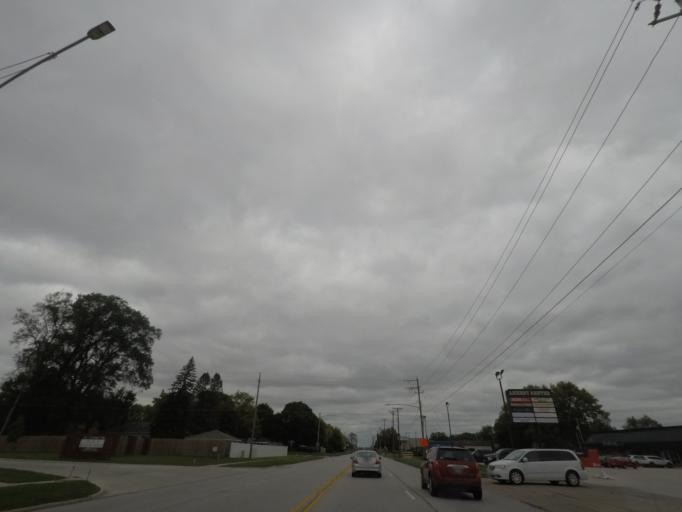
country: US
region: Iowa
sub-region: Polk County
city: Ankeny
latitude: 41.7242
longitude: -93.6004
